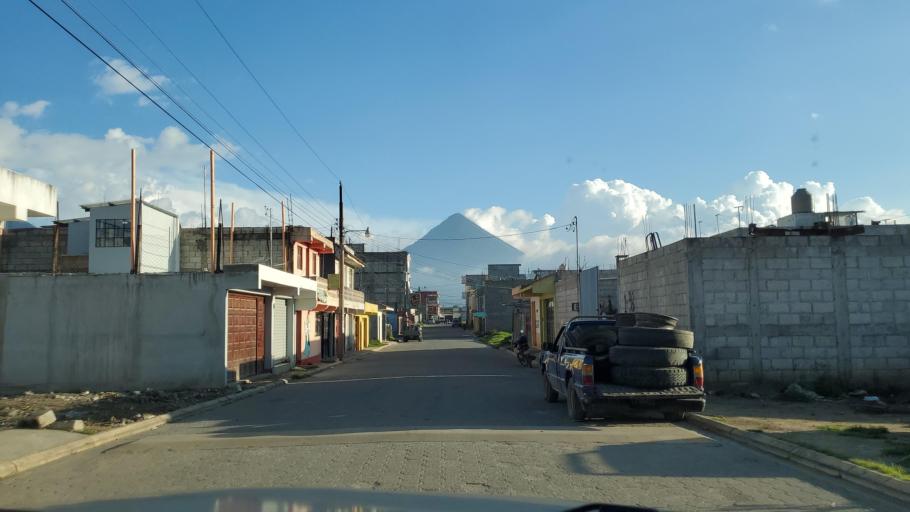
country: GT
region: Quetzaltenango
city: Quetzaltenango
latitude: 14.8370
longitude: -91.5457
